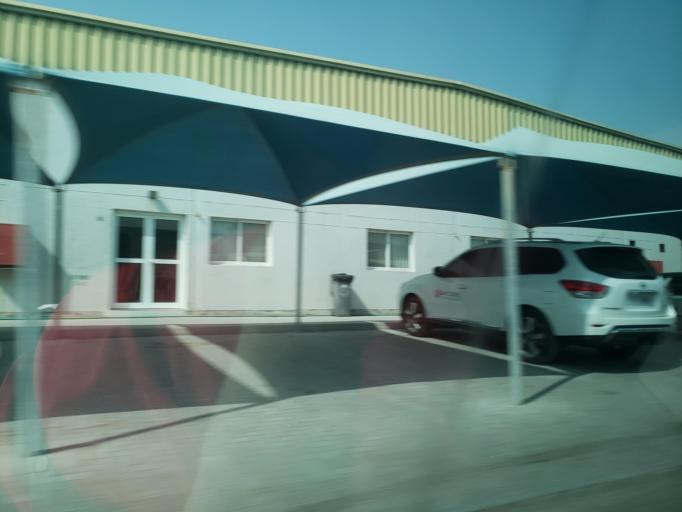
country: AE
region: Ash Shariqah
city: Sharjah
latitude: 25.3321
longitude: 55.4958
